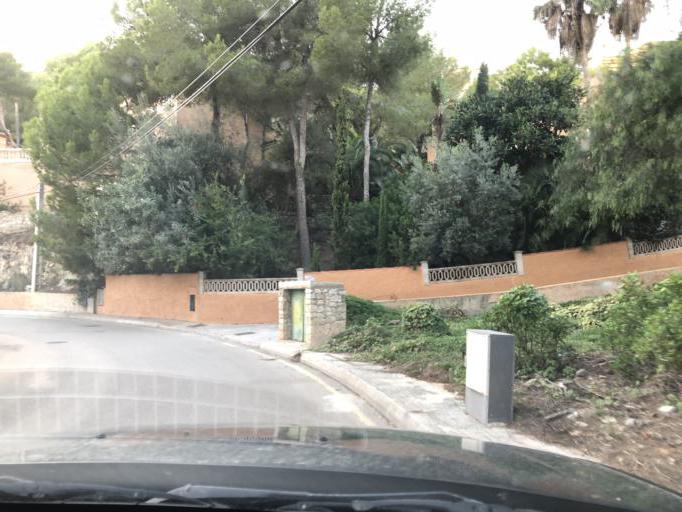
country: ES
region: Balearic Islands
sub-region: Illes Balears
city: Santa Ponsa
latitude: 39.5282
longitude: 2.4670
